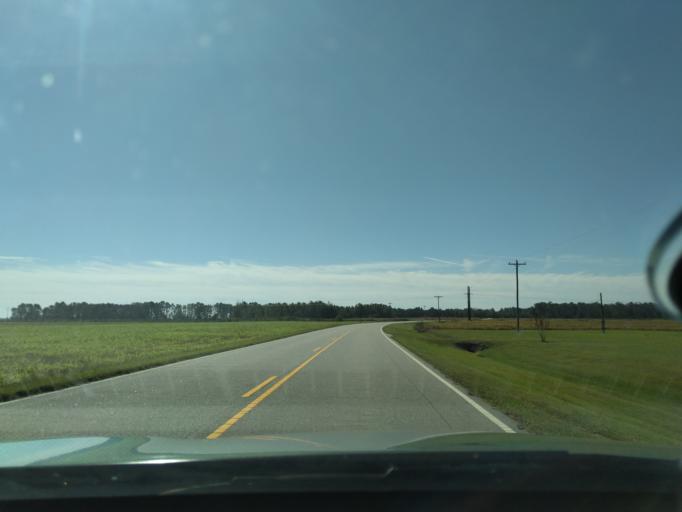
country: US
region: North Carolina
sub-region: Washington County
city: Plymouth
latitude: 35.7429
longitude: -76.7400
